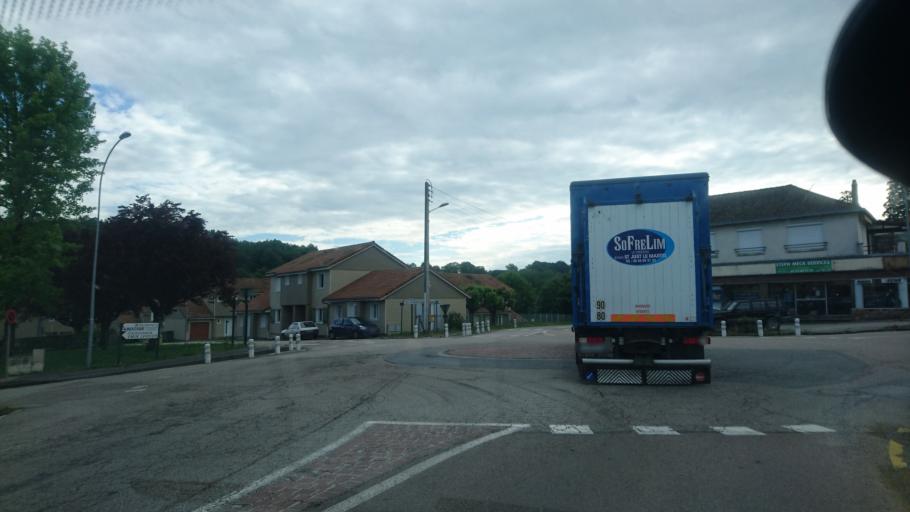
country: FR
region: Limousin
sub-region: Departement de la Haute-Vienne
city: Chateauneuf-la-Foret
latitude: 45.7161
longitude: 1.6071
